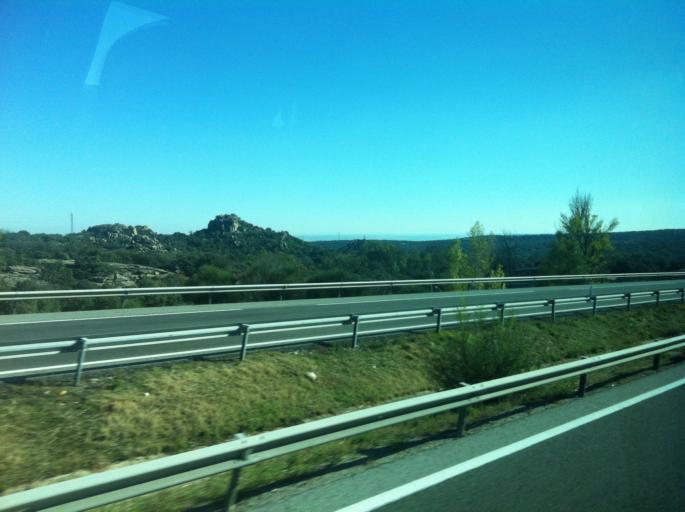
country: ES
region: Madrid
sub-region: Provincia de Madrid
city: La Cabrera
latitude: 40.8655
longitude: -3.6063
